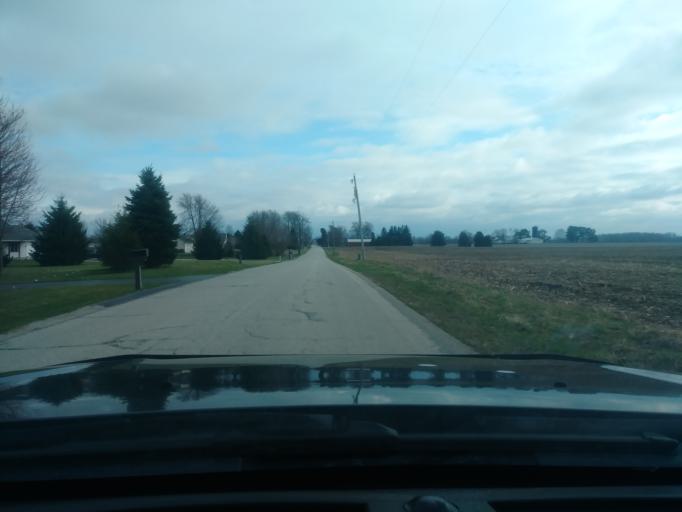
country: US
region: Indiana
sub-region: LaPorte County
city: LaPorte
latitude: 41.5726
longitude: -86.7982
